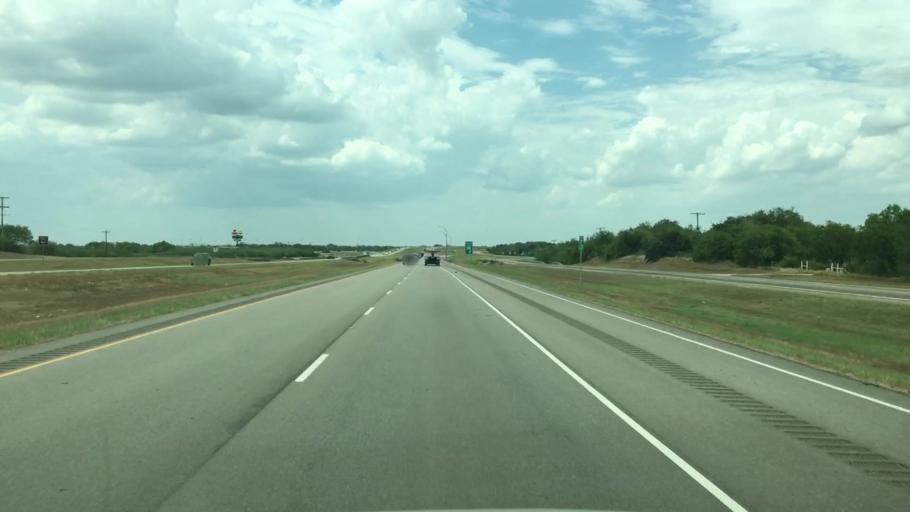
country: US
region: Texas
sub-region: Live Oak County
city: Three Rivers
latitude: 28.5168
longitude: -98.1760
